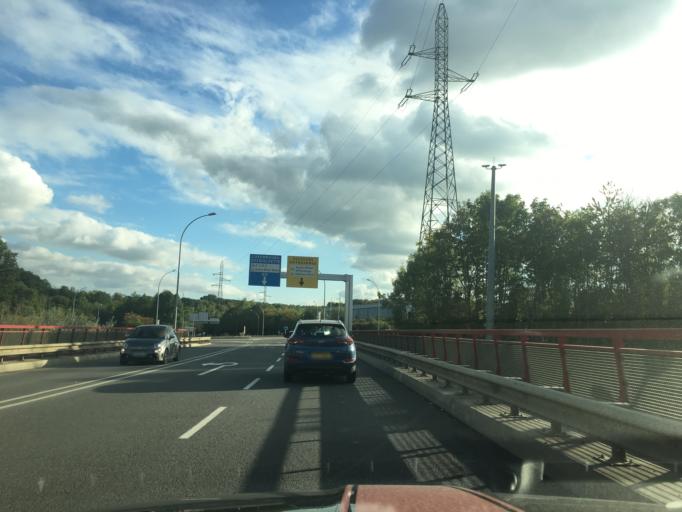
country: LU
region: Luxembourg
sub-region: Canton d'Esch-sur-Alzette
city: Sanem
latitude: 49.5341
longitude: 5.9282
